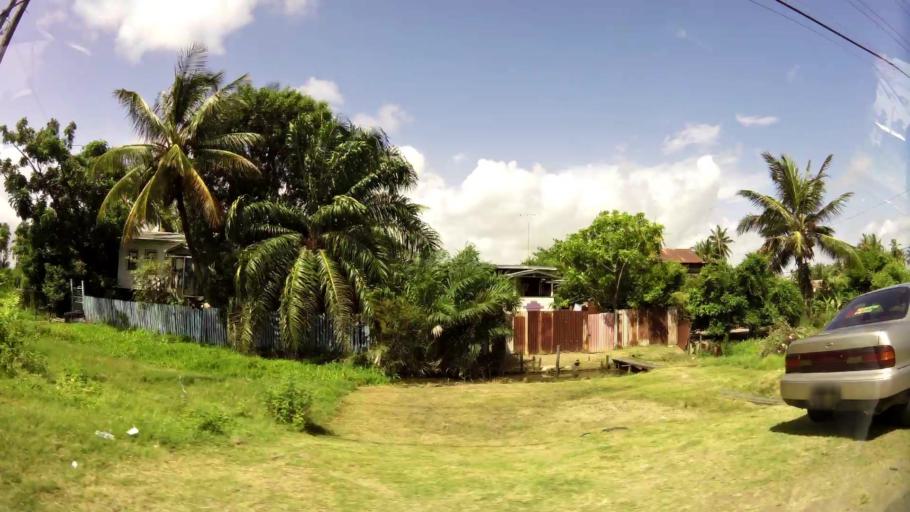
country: GY
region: Demerara-Mahaica
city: Mahaica Village
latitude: 6.7685
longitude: -58.0014
